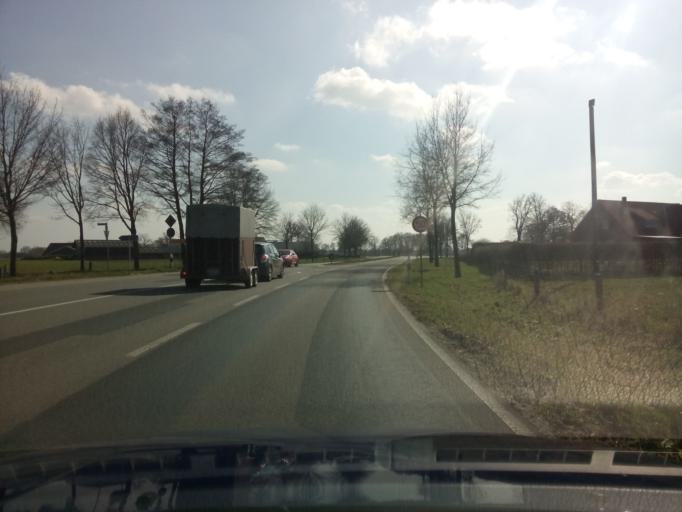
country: DE
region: Lower Saxony
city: Golenkamp
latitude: 52.5396
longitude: 6.9358
